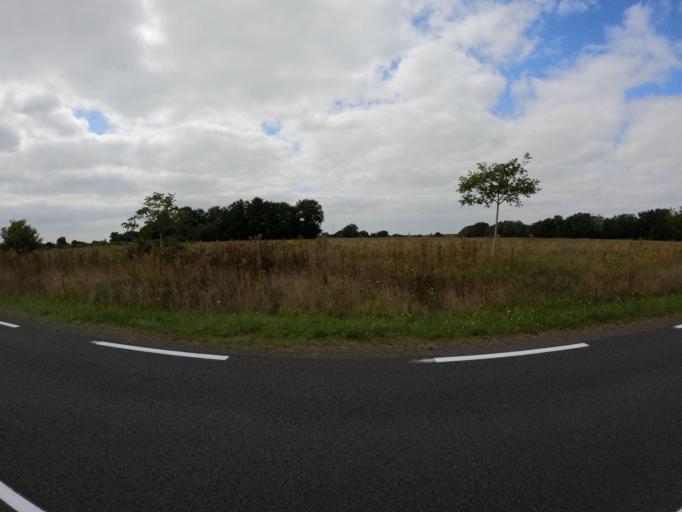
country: FR
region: Poitou-Charentes
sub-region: Departement de la Vienne
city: Charroux
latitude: 46.1458
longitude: 0.4154
